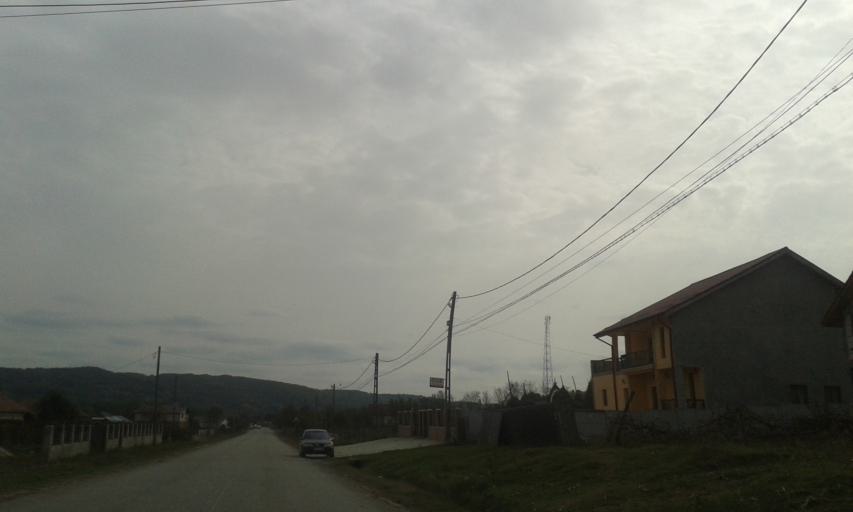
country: RO
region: Gorj
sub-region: Comuna Hurezani
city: Hurezani
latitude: 44.8218
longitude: 23.6495
